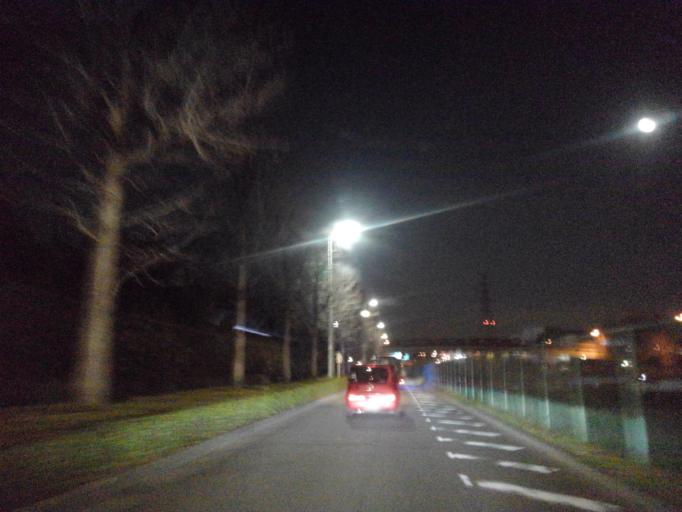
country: JP
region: Tokyo
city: Chofugaoka
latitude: 35.6364
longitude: 139.4885
